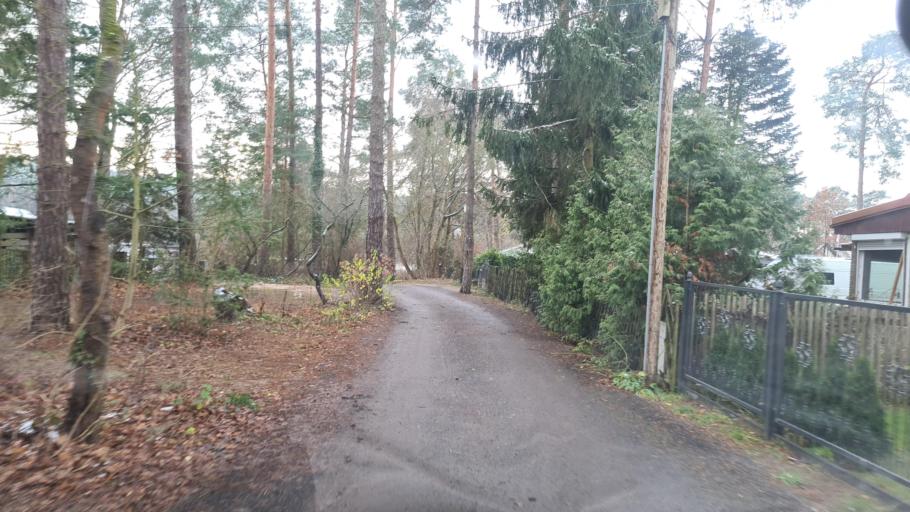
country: DE
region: Brandenburg
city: Grunheide
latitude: 52.4493
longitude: 13.8726
